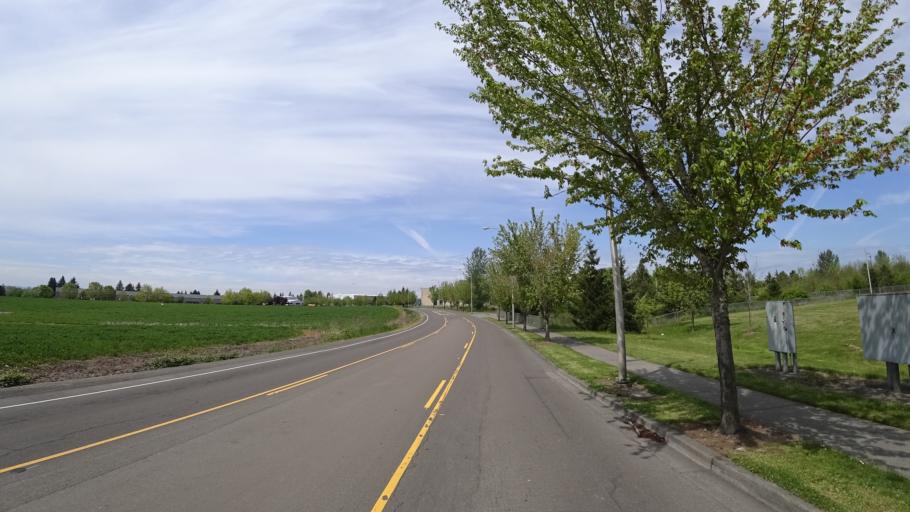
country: US
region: Oregon
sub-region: Washington County
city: Rockcreek
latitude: 45.5600
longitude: -122.9015
